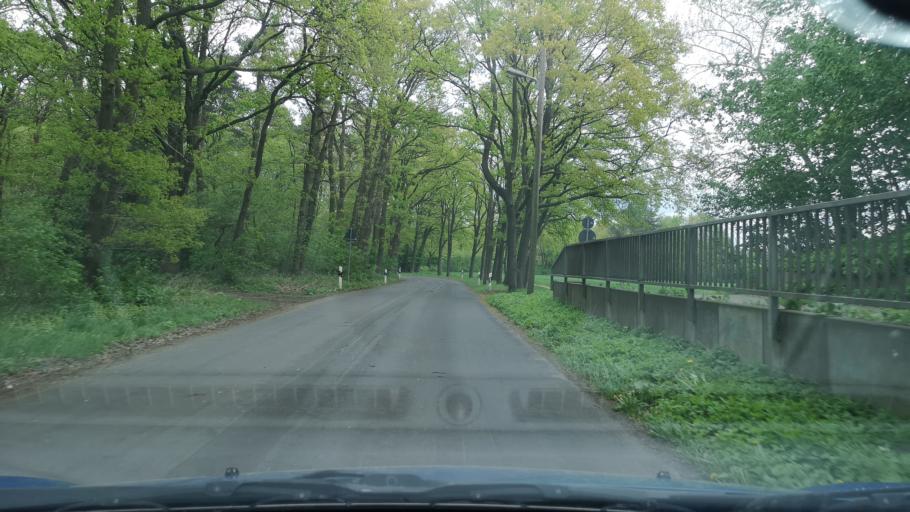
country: DE
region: Lower Saxony
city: Langenhagen
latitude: 52.4708
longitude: 9.7567
